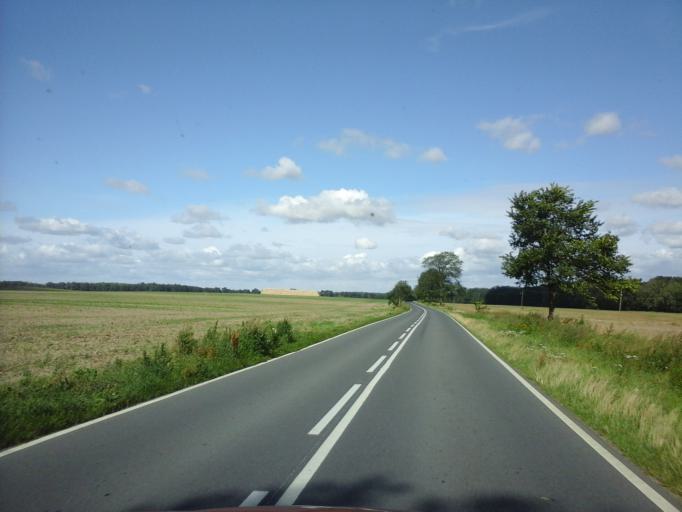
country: PL
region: West Pomeranian Voivodeship
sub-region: Powiat stargardzki
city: Dolice
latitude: 53.1994
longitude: 15.1697
